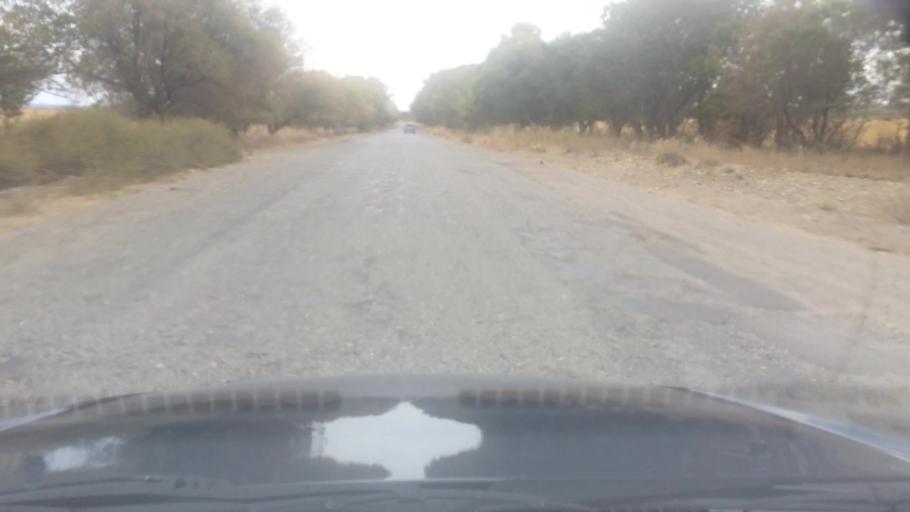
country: KG
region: Ysyk-Koel
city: Balykchy
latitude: 42.3098
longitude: 76.4606
